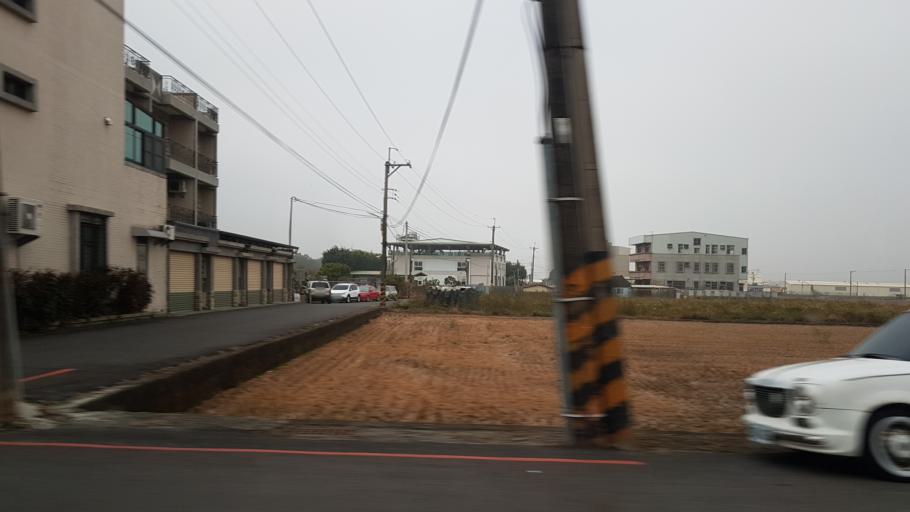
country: TW
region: Taiwan
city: Xinying
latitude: 23.3240
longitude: 120.3161
